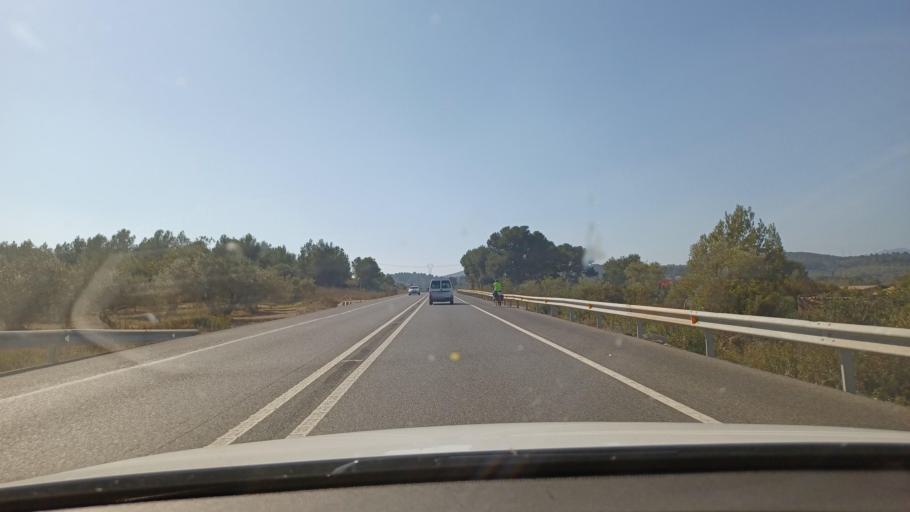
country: ES
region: Catalonia
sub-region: Provincia de Tarragona
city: El Perello
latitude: 40.8911
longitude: 0.7258
